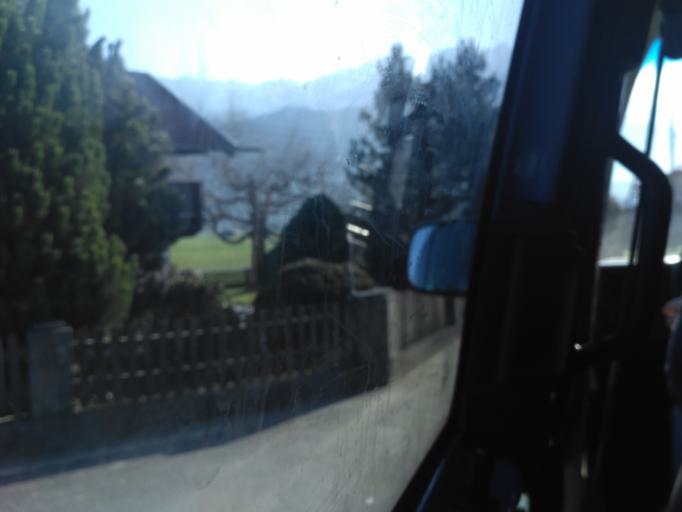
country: AT
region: Salzburg
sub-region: Politischer Bezirk Zell am See
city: Leogang
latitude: 47.4472
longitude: 12.8055
